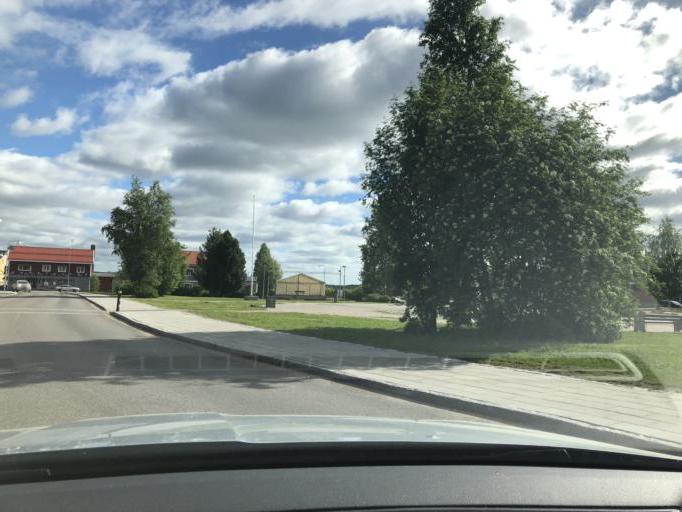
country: SE
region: Norrbotten
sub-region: Pajala Kommun
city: Pajala
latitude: 67.2125
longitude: 23.3657
